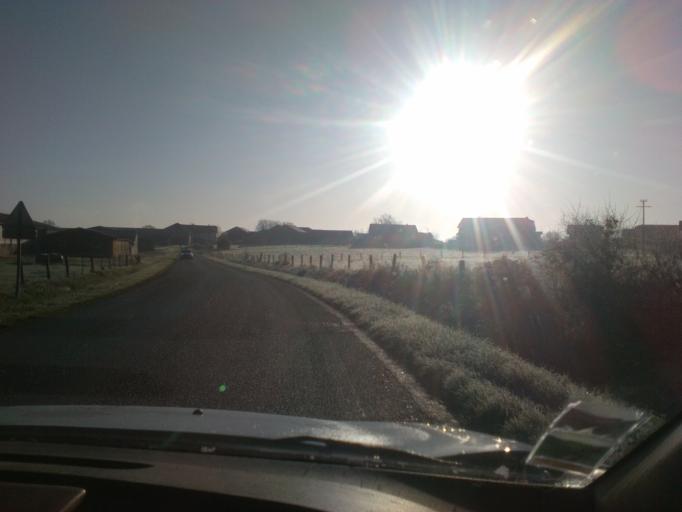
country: FR
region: Lorraine
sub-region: Departement des Vosges
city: Uzemain
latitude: 48.1385
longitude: 6.2534
